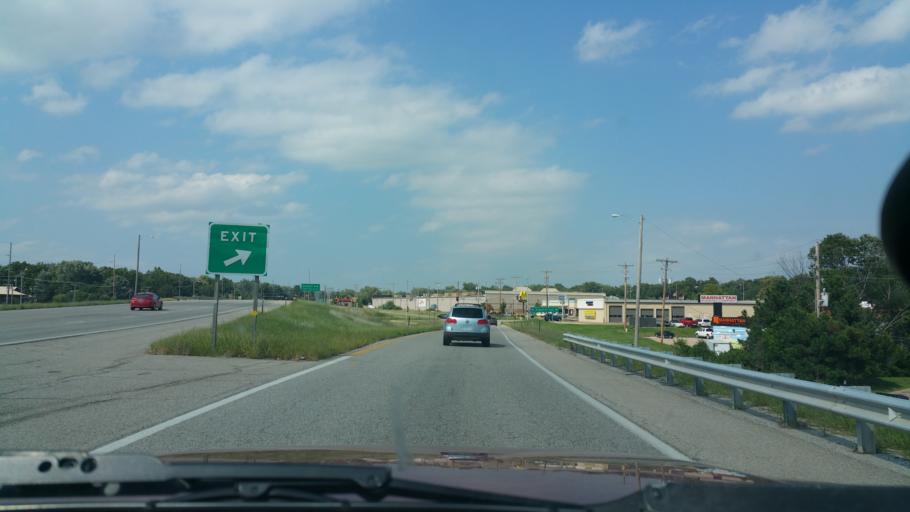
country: US
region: Kansas
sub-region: Riley County
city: Manhattan
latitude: 39.1878
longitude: -96.6112
